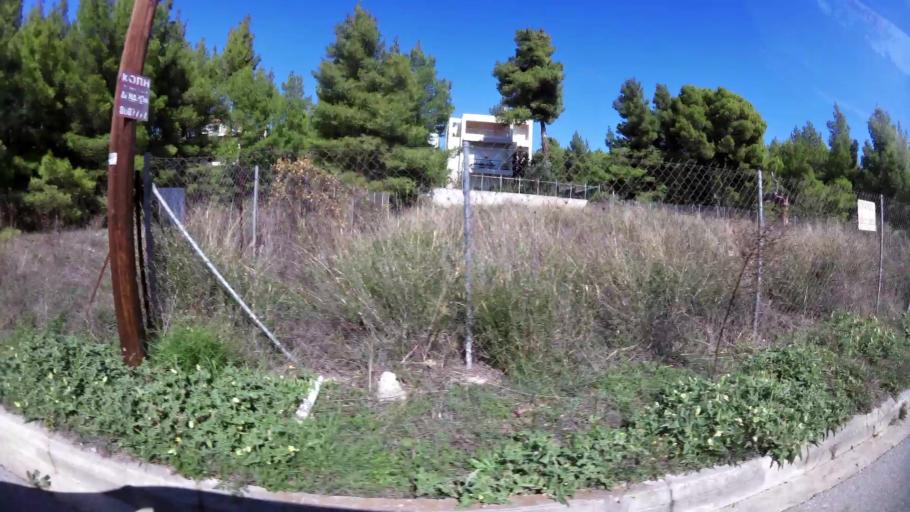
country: GR
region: Attica
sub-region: Nomarchia Anatolikis Attikis
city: Dioni
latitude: 38.0221
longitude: 23.9304
